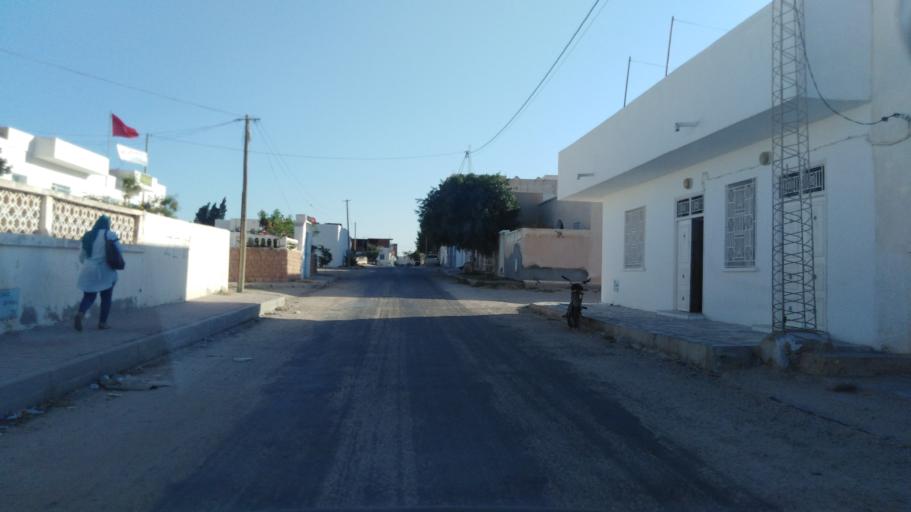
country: TN
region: Qabis
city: Gabes
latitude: 33.9556
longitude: 10.0097
